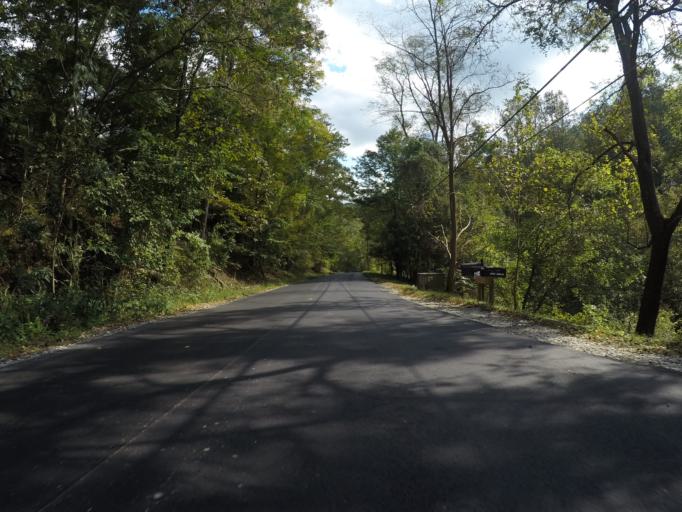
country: US
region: West Virginia
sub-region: Wayne County
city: Lavalette
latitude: 38.3652
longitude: -82.4304
